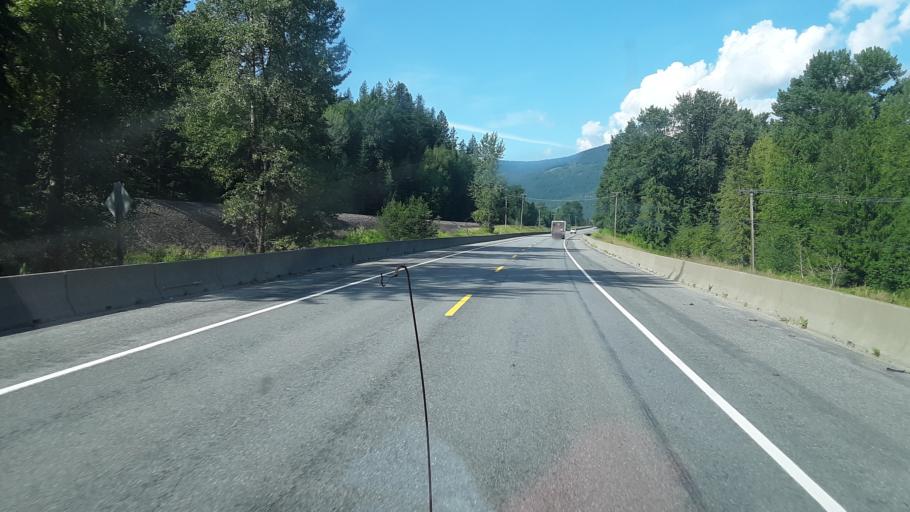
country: US
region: Idaho
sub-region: Bonner County
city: Ponderay
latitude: 48.4185
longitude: -116.5047
